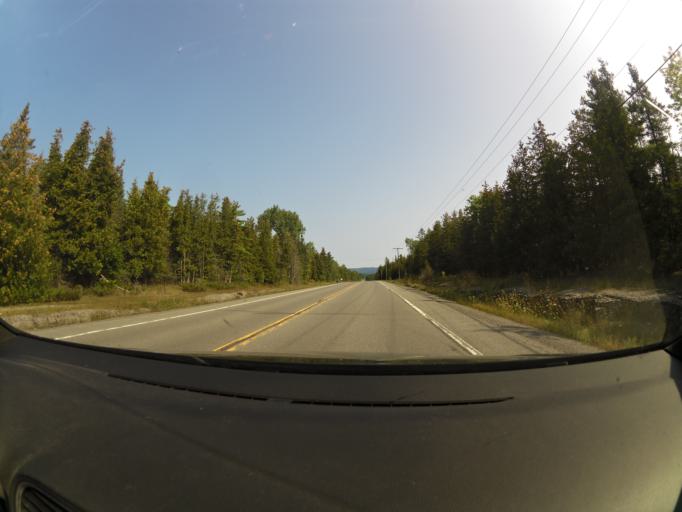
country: CA
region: Ontario
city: Arnprior
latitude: 45.4826
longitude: -76.1596
